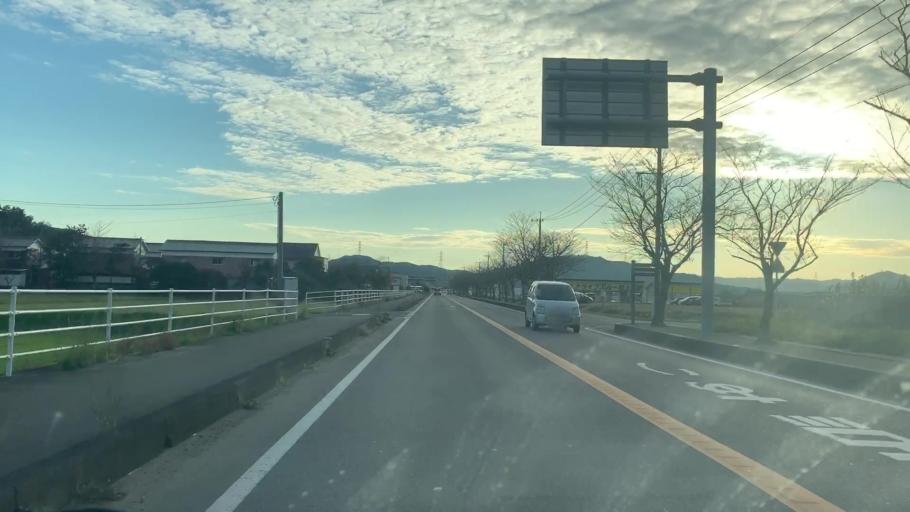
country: JP
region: Saga Prefecture
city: Karatsu
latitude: 33.4134
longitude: 129.9937
